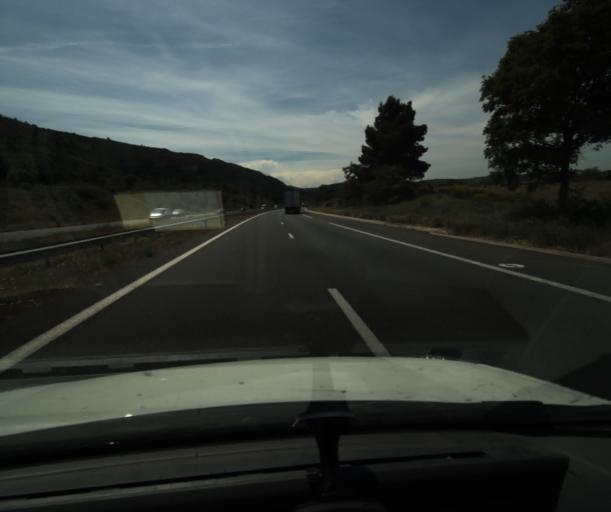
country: FR
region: Languedoc-Roussillon
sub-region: Departement de l'Aude
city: Capendu
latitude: 43.1785
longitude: 2.5037
